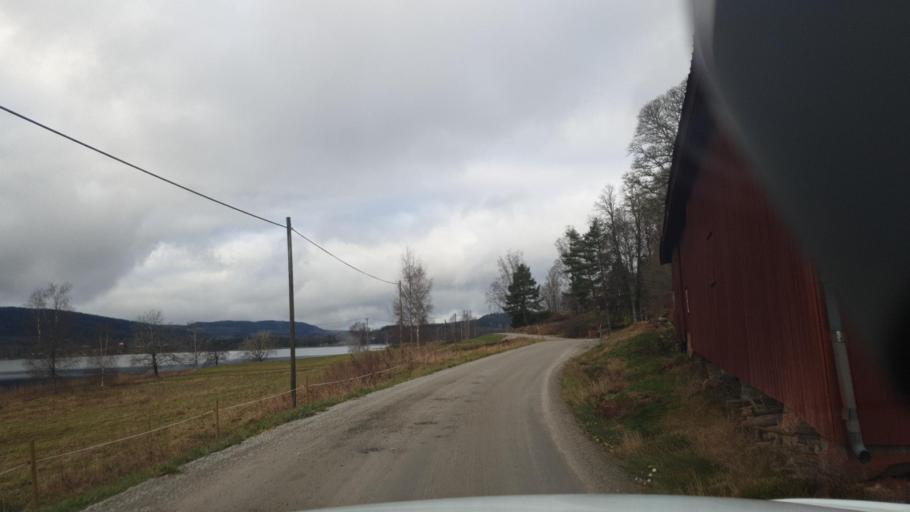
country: SE
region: Vaermland
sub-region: Arvika Kommun
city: Arvika
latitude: 59.7285
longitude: 12.8346
